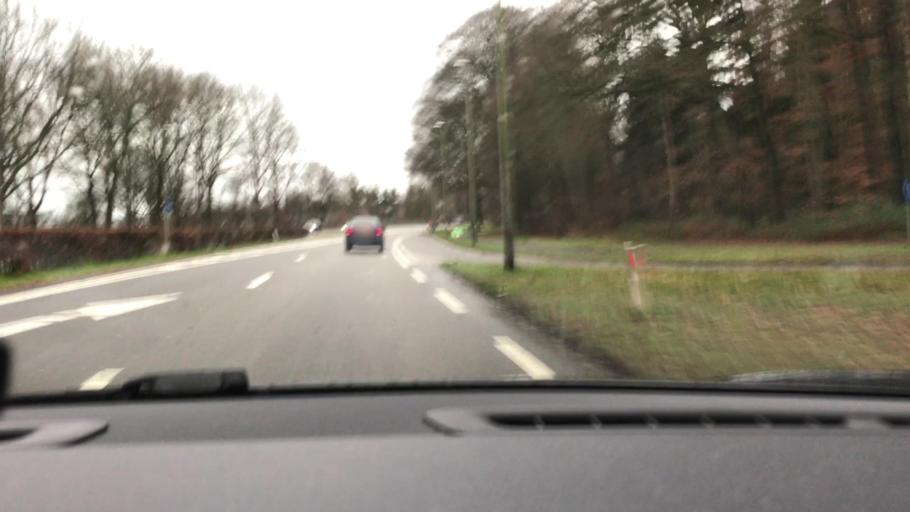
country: NL
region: Gelderland
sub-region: Gemeente Arnhem
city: Arnhem
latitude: 52.0086
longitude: 5.9254
